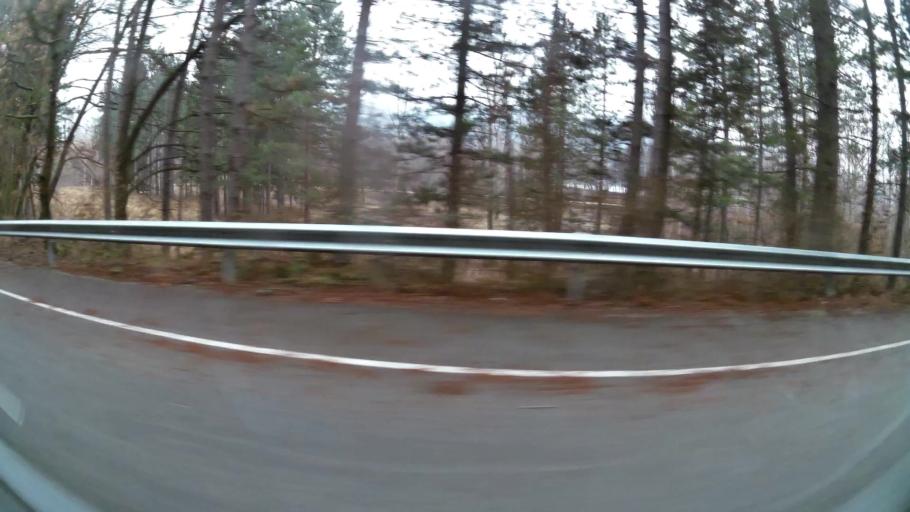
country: BG
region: Sofia-Capital
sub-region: Stolichna Obshtina
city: Sofia
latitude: 42.5869
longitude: 23.4270
